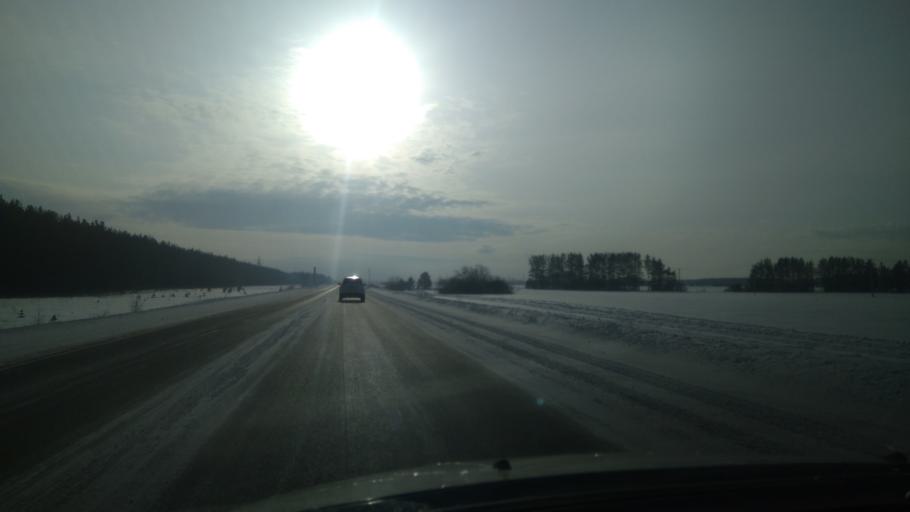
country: RU
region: Sverdlovsk
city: Sukhoy Log
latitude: 56.8708
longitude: 62.0464
